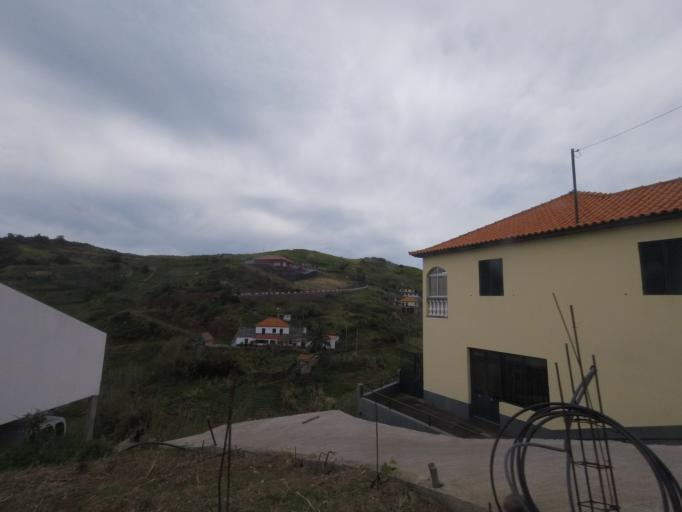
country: PT
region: Madeira
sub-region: Santana
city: Santana
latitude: 32.7652
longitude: -16.8164
